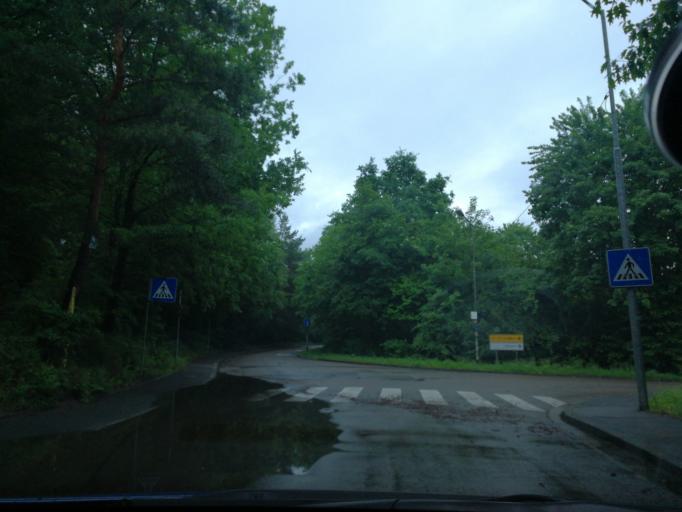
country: DE
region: Rheinland-Pfalz
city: Kaiserslautern
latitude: 49.4385
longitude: 7.8104
